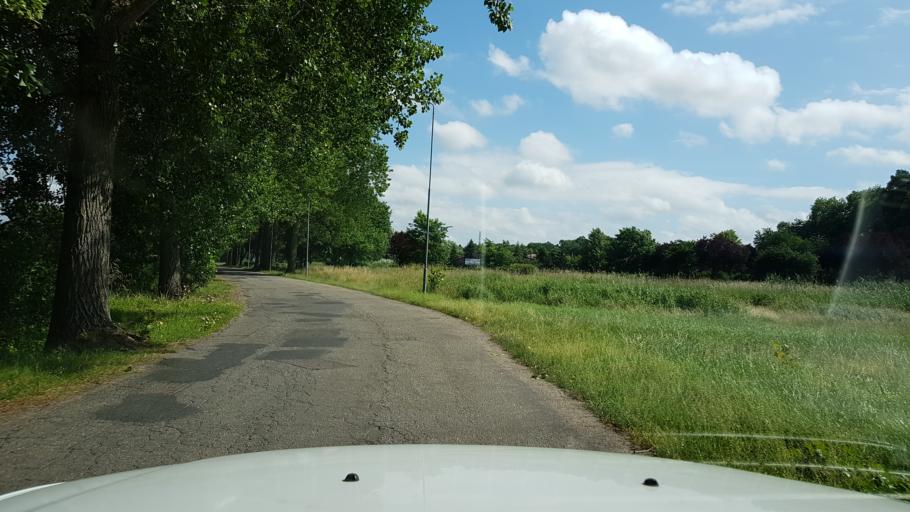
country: PL
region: West Pomeranian Voivodeship
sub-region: Powiat kamienski
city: Kamien Pomorski
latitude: 53.9715
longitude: 14.7792
